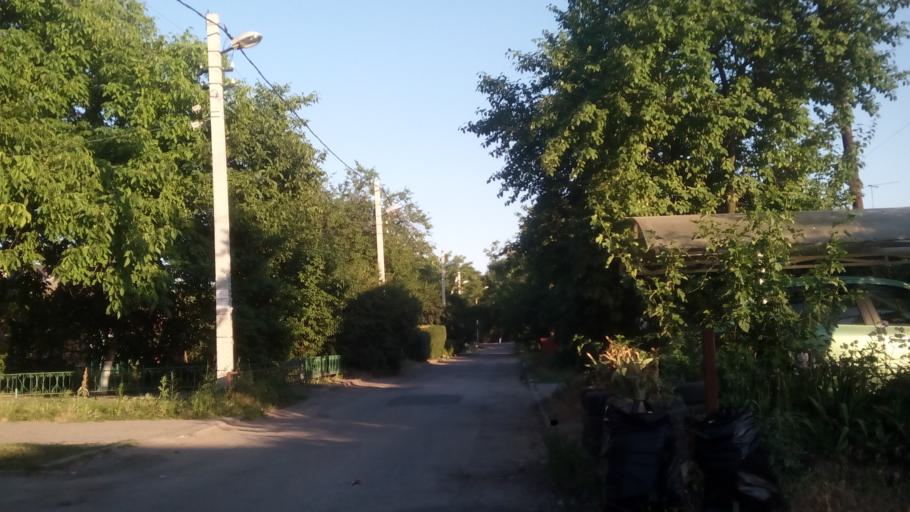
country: RU
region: Rostov
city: Imeni Chkalova
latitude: 47.2472
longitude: 39.7710
